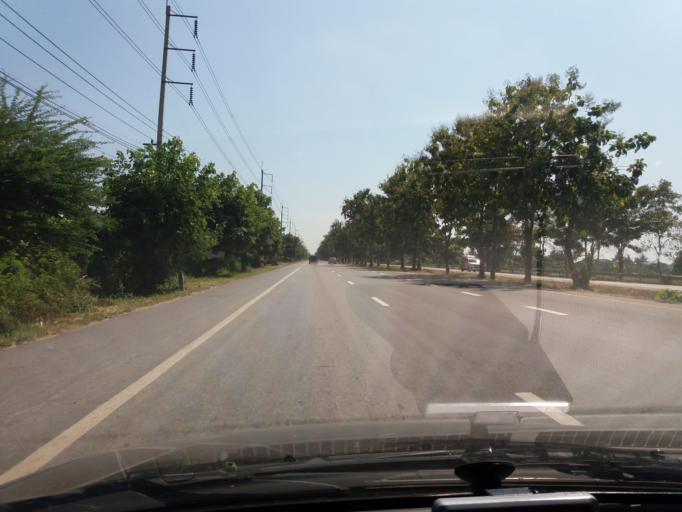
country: TH
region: Chai Nat
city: Sankhaburi
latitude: 15.0987
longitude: 100.1372
